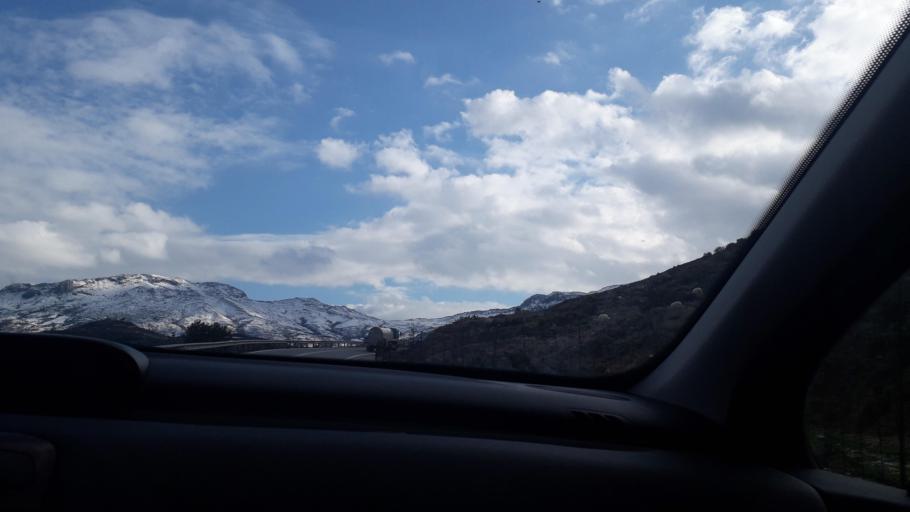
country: GR
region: Crete
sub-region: Nomos Rethymnis
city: Agia Foteini
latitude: 35.2700
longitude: 24.5637
